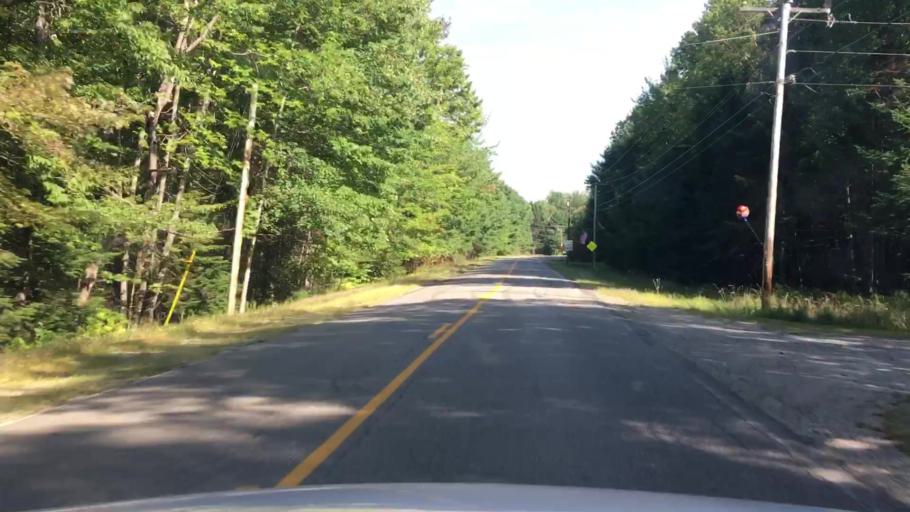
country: US
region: Maine
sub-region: Penobscot County
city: Enfield
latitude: 45.2375
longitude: -68.5483
